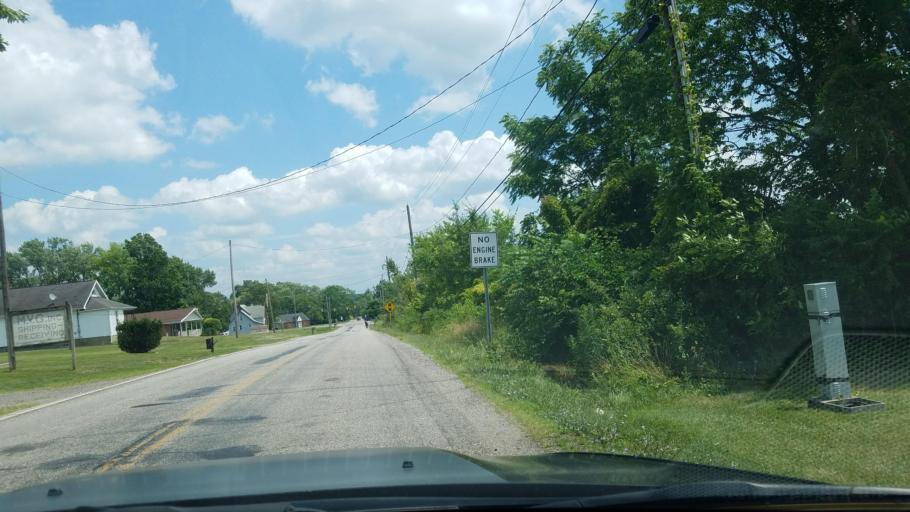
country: US
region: Ohio
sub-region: Trumbull County
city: Bolindale
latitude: 41.2032
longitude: -80.7827
